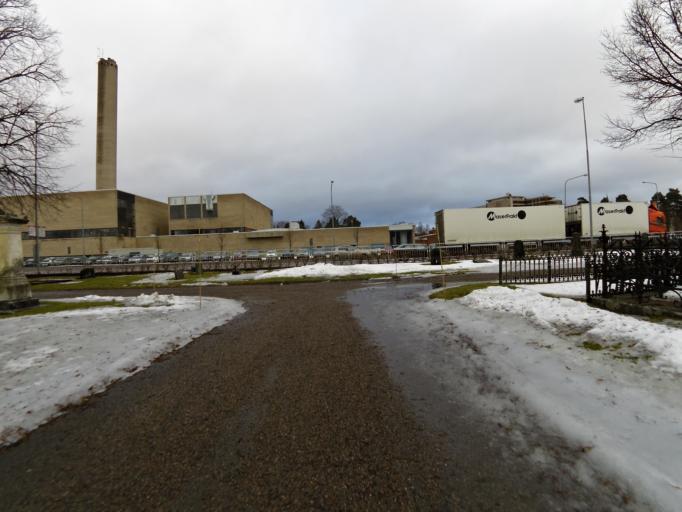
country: SE
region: Gaevleborg
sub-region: Gavle Kommun
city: Gavle
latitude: 60.6751
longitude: 17.1154
